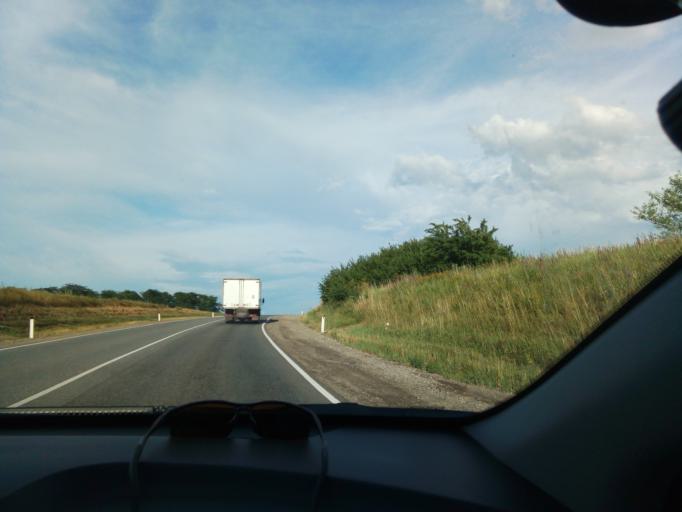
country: RU
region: Krasnodarskiy
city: Chamlykskaya
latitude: 44.7398
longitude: 40.8475
